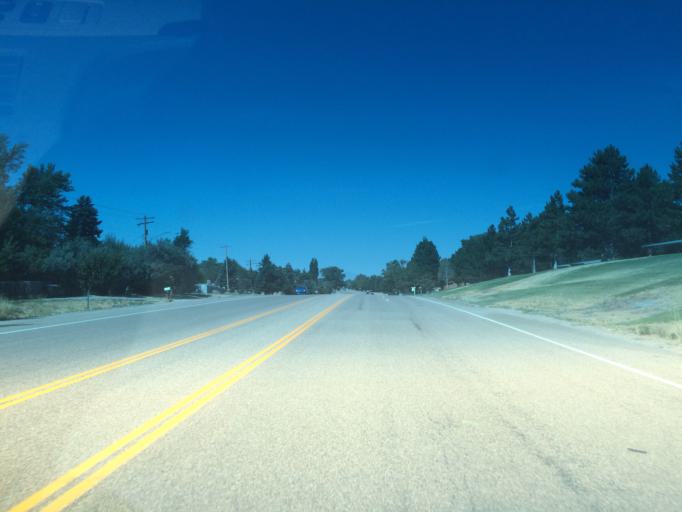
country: US
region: Utah
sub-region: Weber County
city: Ogden
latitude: 41.2392
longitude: -111.9334
